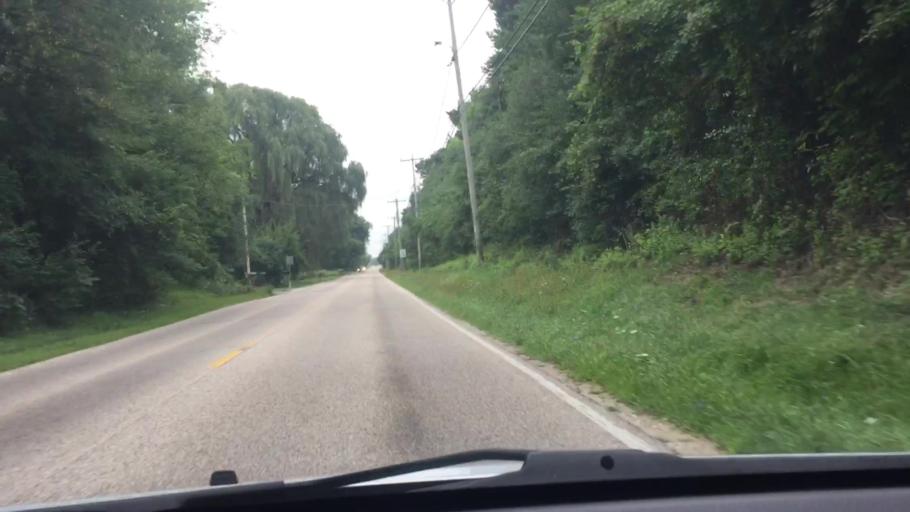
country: US
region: Wisconsin
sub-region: Waukesha County
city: Delafield
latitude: 43.0522
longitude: -88.4424
